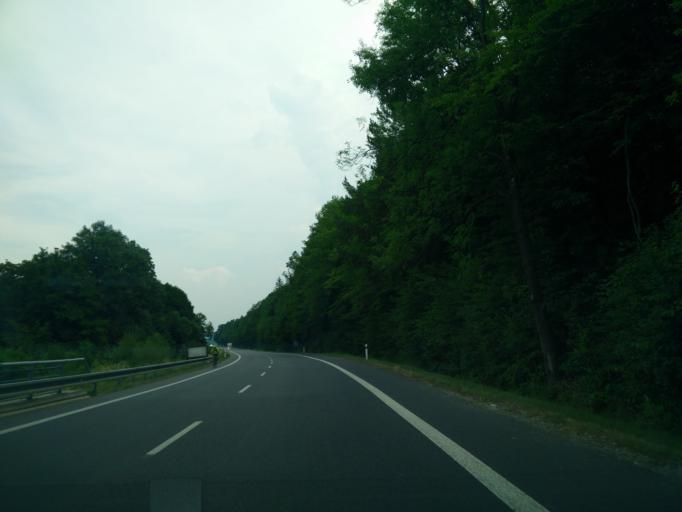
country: SK
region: Nitriansky
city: Handlova
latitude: 48.6493
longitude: 18.7584
